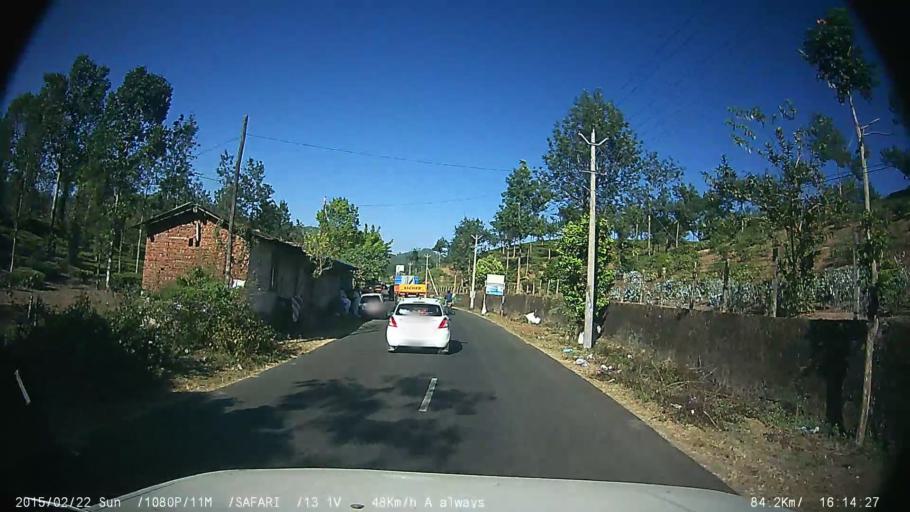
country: IN
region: Tamil Nadu
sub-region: Theni
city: Gudalur
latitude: 9.5823
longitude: 77.1011
